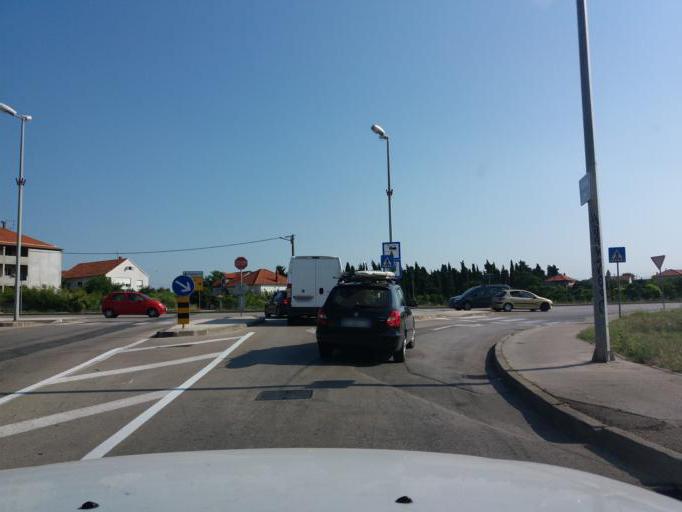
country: HR
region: Zadarska
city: Zadar
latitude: 44.1013
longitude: 15.2559
